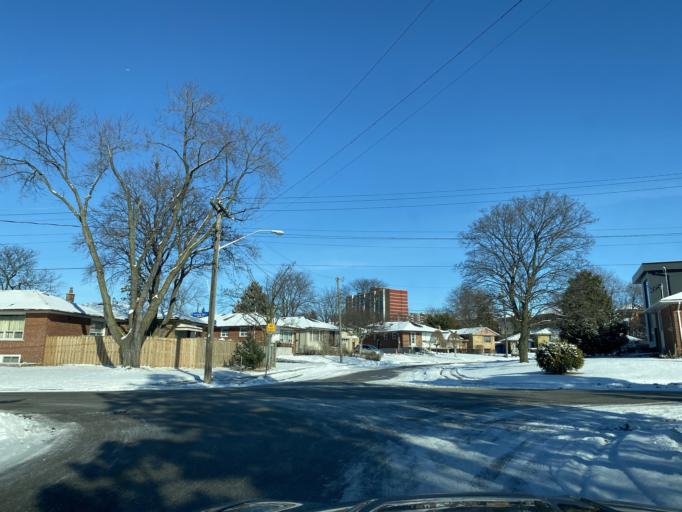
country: CA
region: Ontario
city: Scarborough
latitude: 43.7731
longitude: -79.3127
